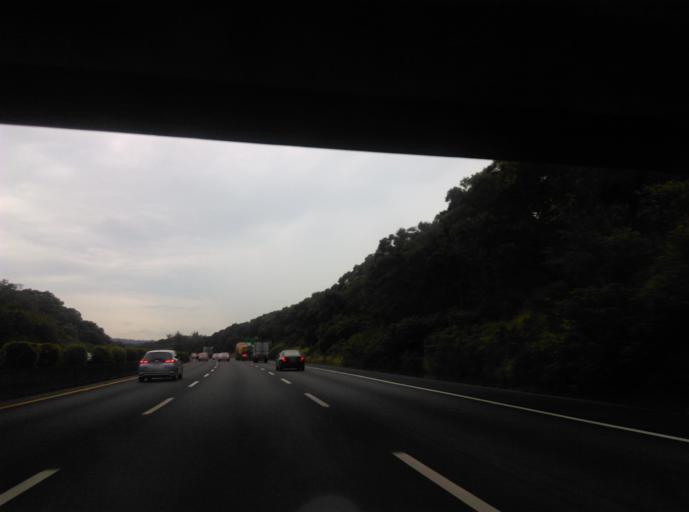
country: TW
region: Taiwan
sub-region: Hsinchu
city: Hsinchu
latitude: 24.7523
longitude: 120.9329
